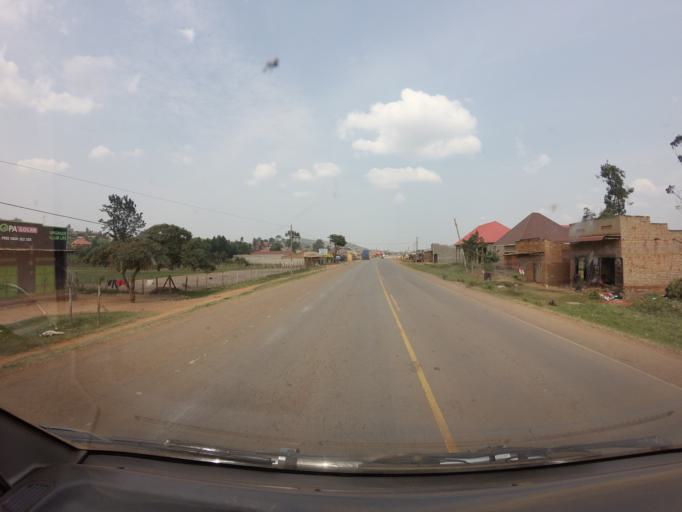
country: UG
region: Central Region
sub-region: Lwengo District
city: Lwengo
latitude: -0.3840
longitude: 31.3123
